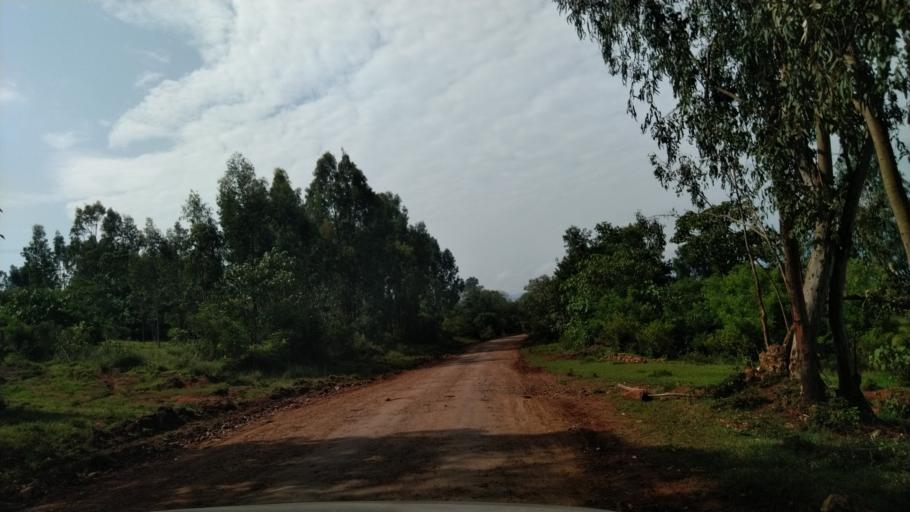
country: ET
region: Oromiya
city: Jima
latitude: 7.6685
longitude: 37.2440
